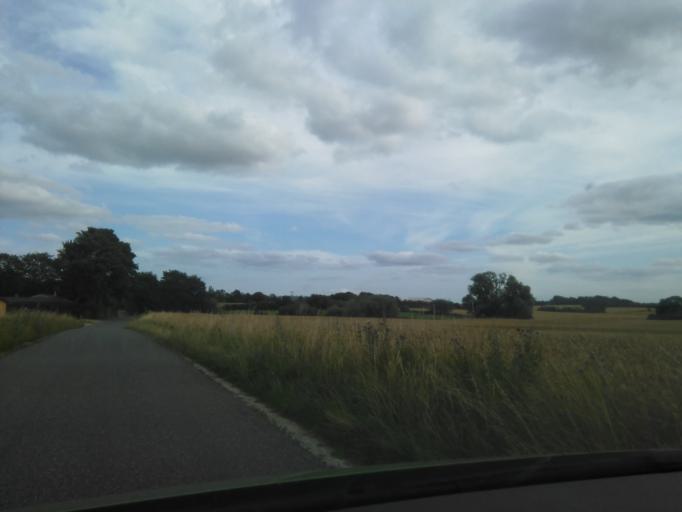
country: DK
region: Central Jutland
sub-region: Arhus Kommune
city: Tranbjerg
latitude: 56.0589
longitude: 10.1213
